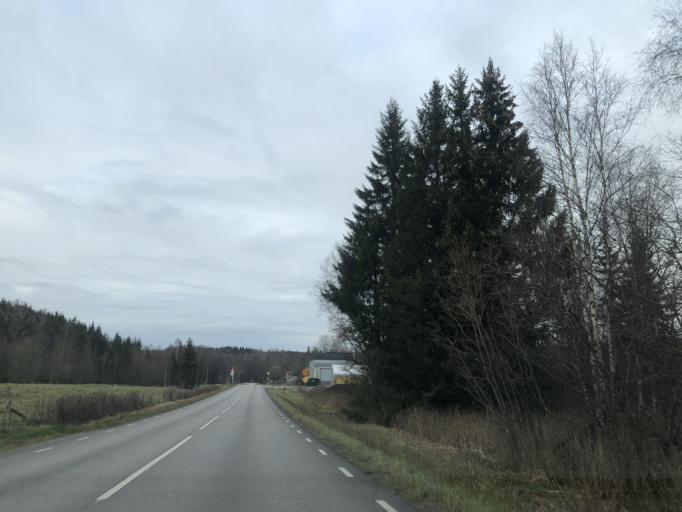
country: SE
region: Vaestra Goetaland
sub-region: Ulricehamns Kommun
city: Ulricehamn
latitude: 57.6749
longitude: 13.4014
